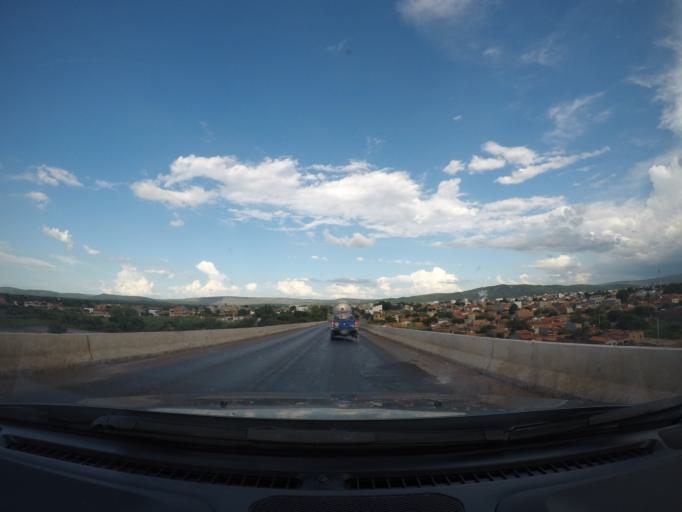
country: BR
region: Bahia
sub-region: Ibotirama
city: Ibotirama
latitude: -12.1796
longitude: -43.2241
